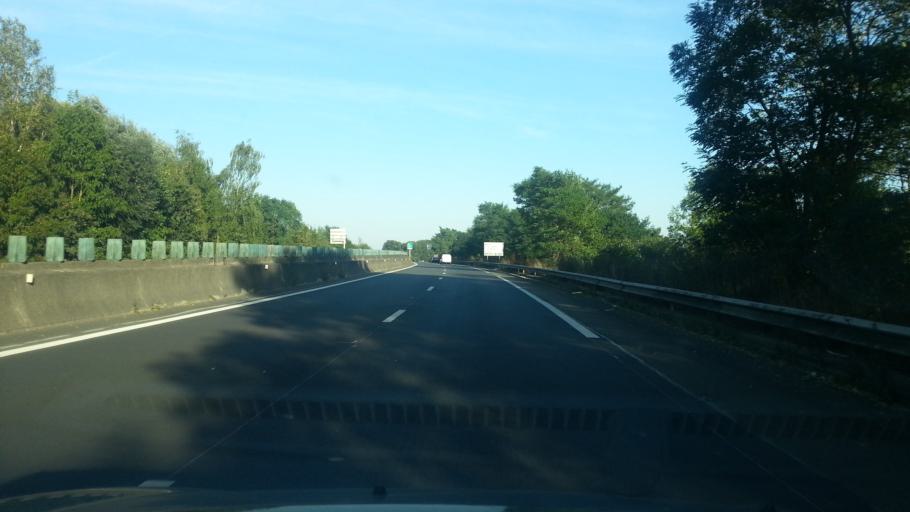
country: FR
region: Picardie
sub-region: Departement de l'Oise
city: Clermont
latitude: 49.3893
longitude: 2.4031
